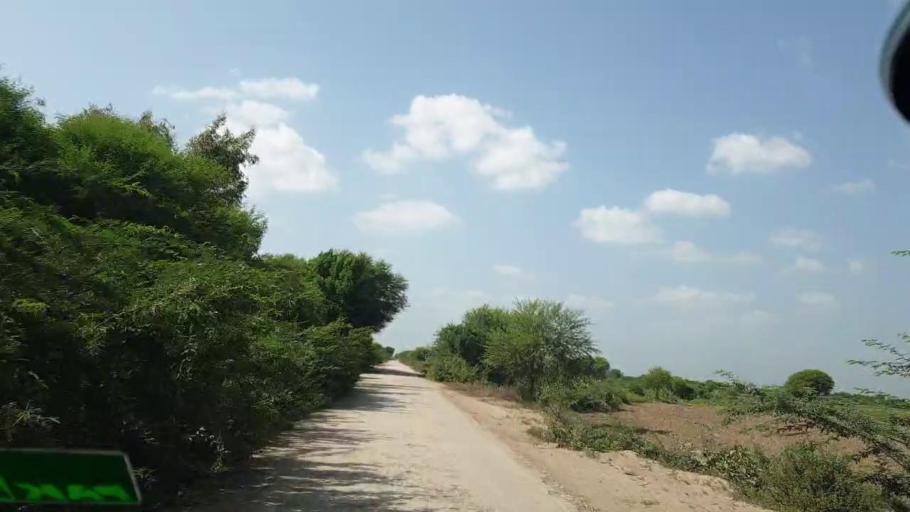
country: PK
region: Sindh
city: Naukot
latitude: 24.6453
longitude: 69.2236
